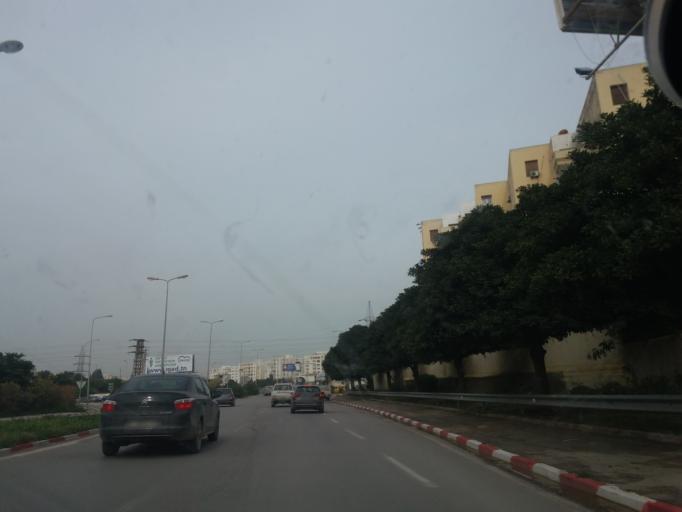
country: TN
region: Tunis
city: Tunis
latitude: 36.8499
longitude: 10.1560
